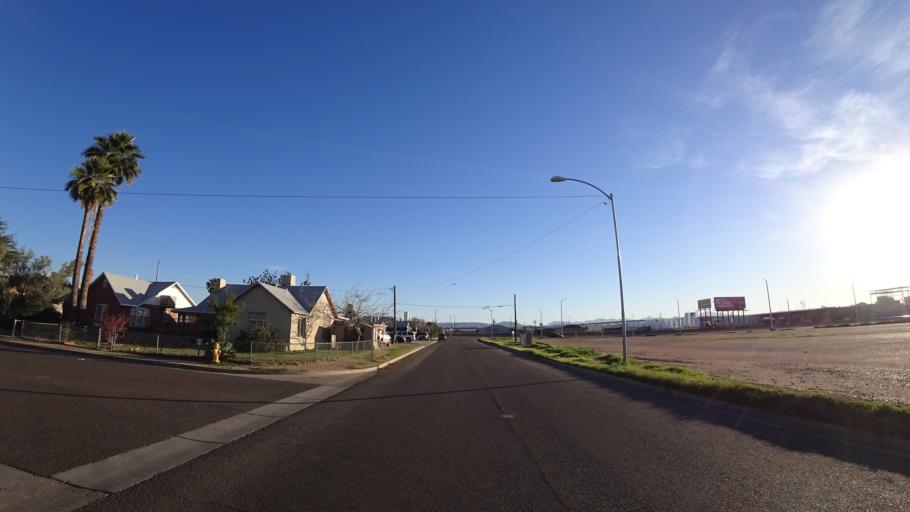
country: US
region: Arizona
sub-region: Maricopa County
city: Phoenix
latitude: 33.4694
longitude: -112.1025
